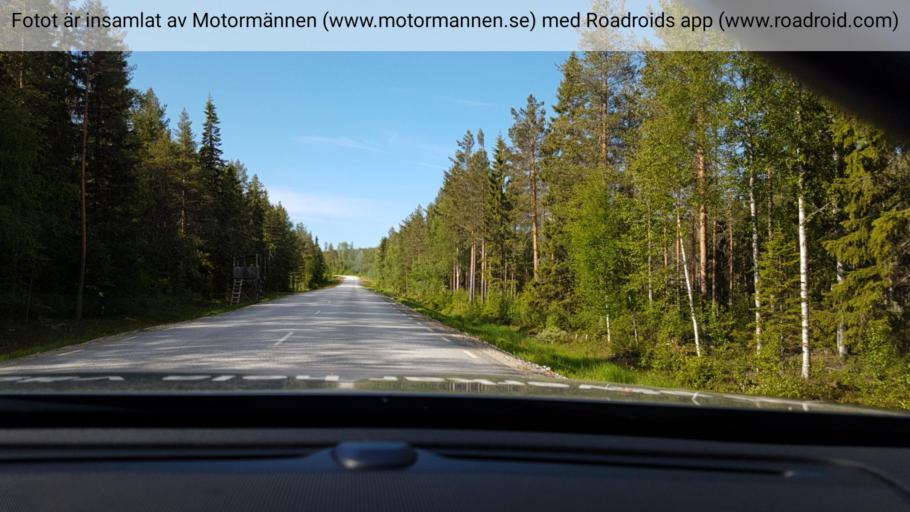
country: SE
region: Vaesterbotten
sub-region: Vindelns Kommun
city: Vindeln
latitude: 64.1898
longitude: 19.4068
